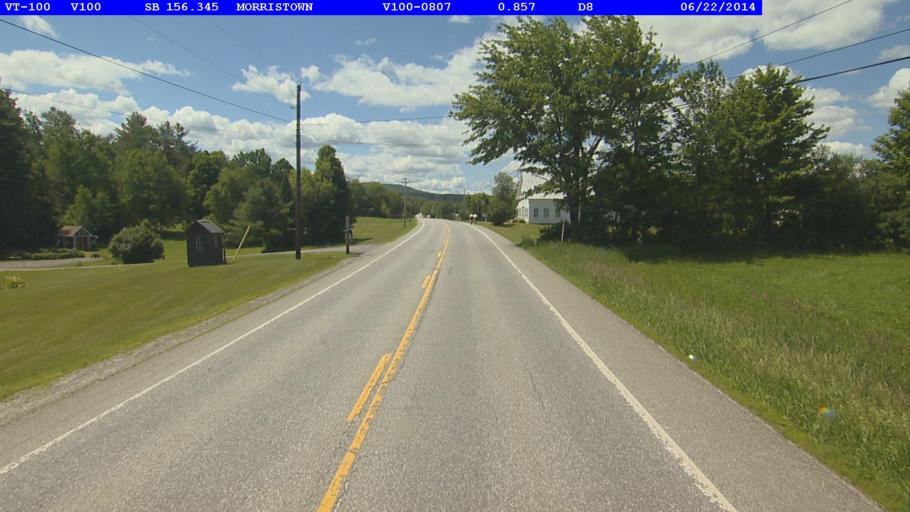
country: US
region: Vermont
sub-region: Lamoille County
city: Morristown
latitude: 44.5058
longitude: -72.6268
